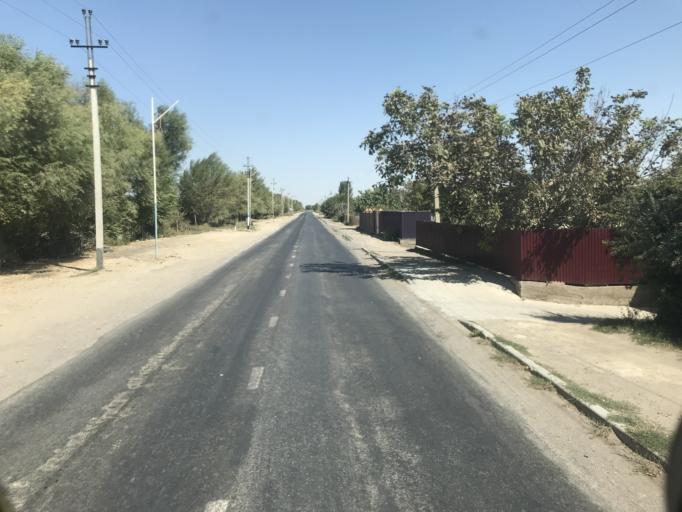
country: KZ
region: Ongtustik Qazaqstan
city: Ilyich
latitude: 40.9388
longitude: 68.4883
